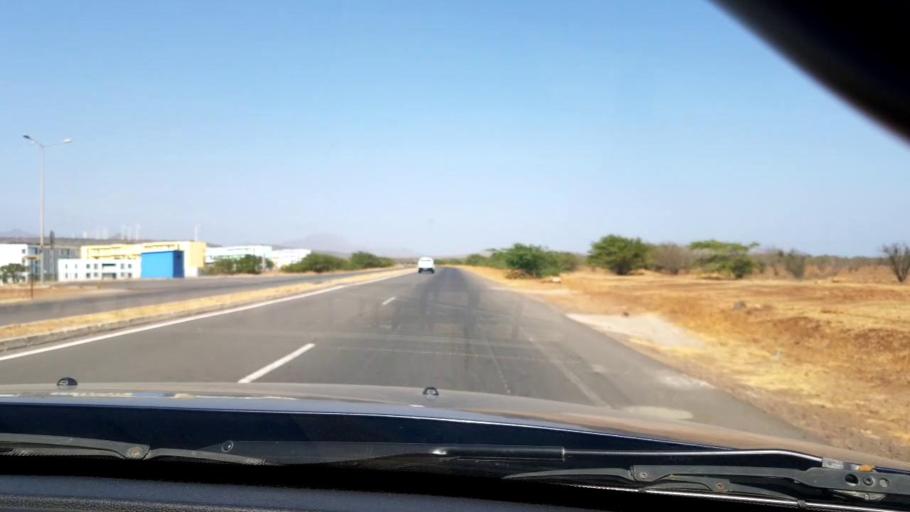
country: CV
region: Praia
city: Praia
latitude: 14.9482
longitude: -23.4907
